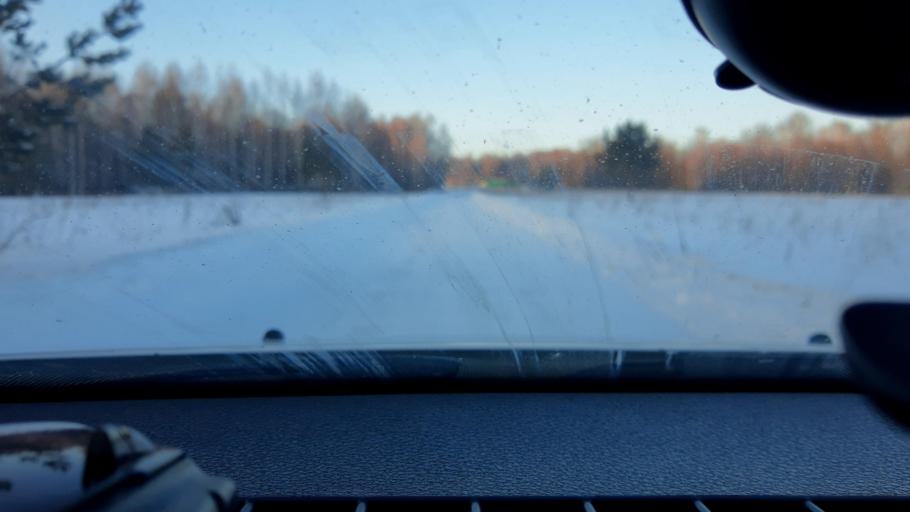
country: RU
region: Bashkortostan
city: Kudeyevskiy
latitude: 54.8097
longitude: 56.6767
